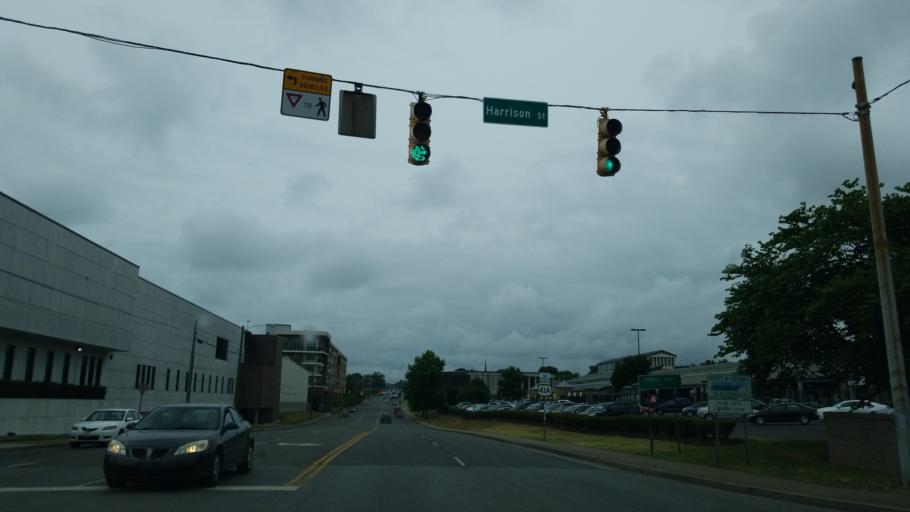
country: US
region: Tennessee
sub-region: Davidson County
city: Nashville
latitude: 36.1686
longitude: -86.7883
